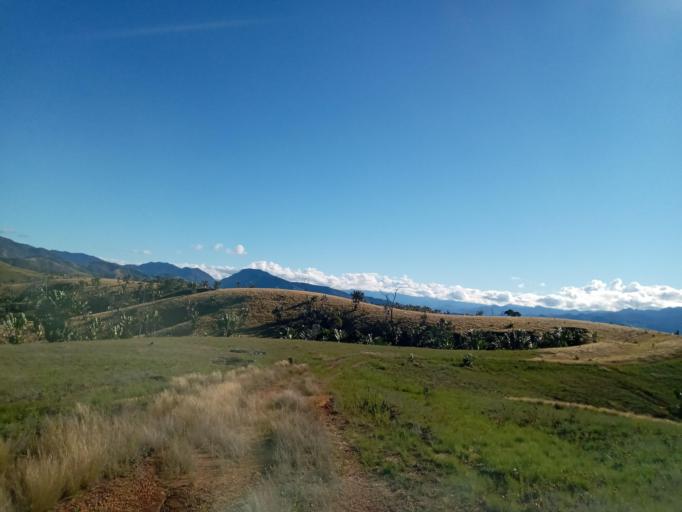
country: MG
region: Anosy
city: Fort Dauphin
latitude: -24.4073
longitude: 47.2534
